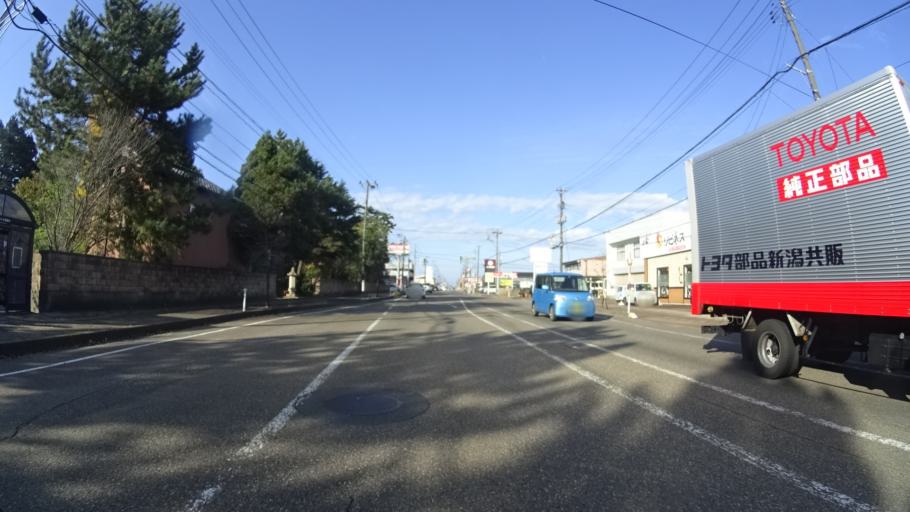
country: JP
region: Niigata
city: Joetsu
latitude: 37.1531
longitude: 138.2384
